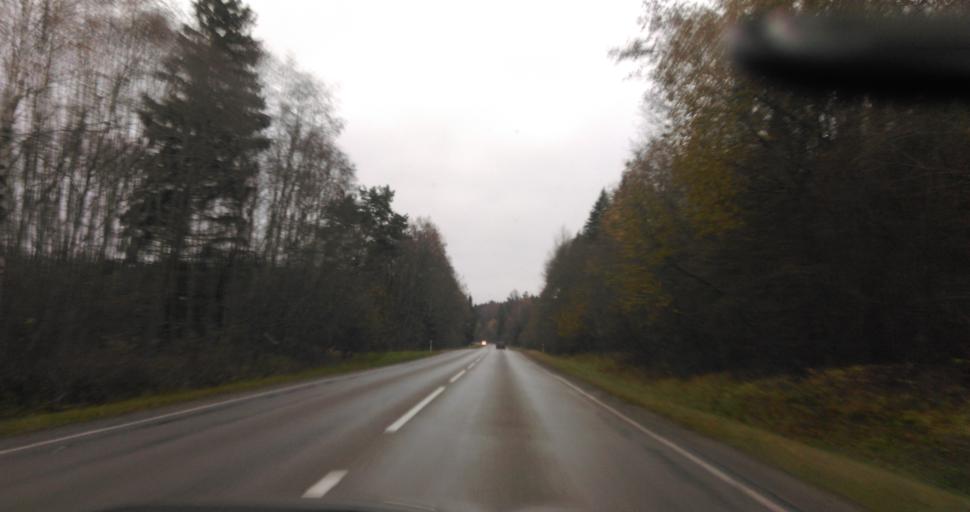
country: LT
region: Panevezys
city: Rokiskis
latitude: 55.8611
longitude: 25.5428
